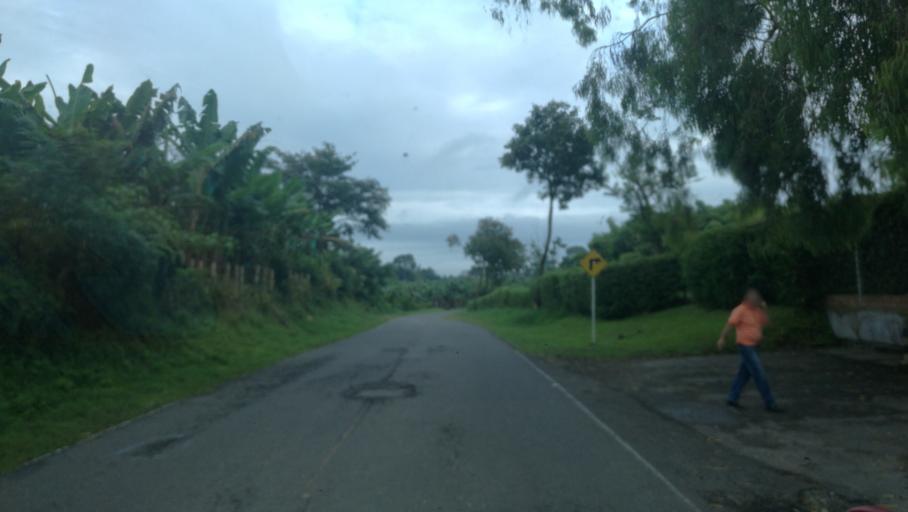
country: CO
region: Quindio
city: Montenegro
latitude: 4.5327
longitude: -75.7743
